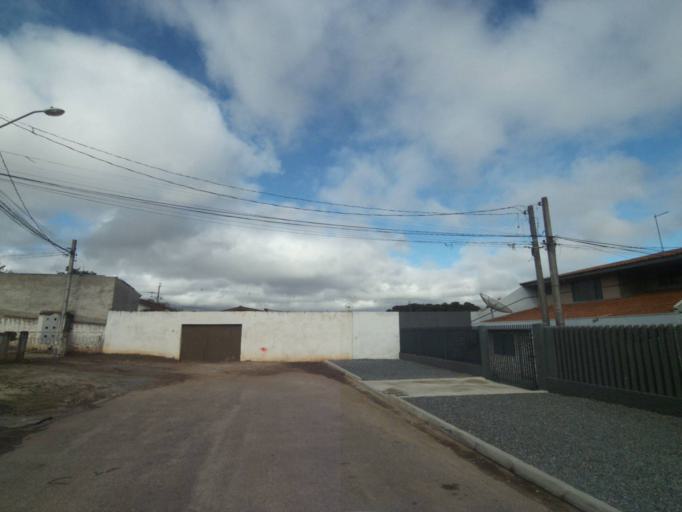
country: BR
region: Parana
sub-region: Sao Jose Dos Pinhais
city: Sao Jose dos Pinhais
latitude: -25.5231
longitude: -49.3013
